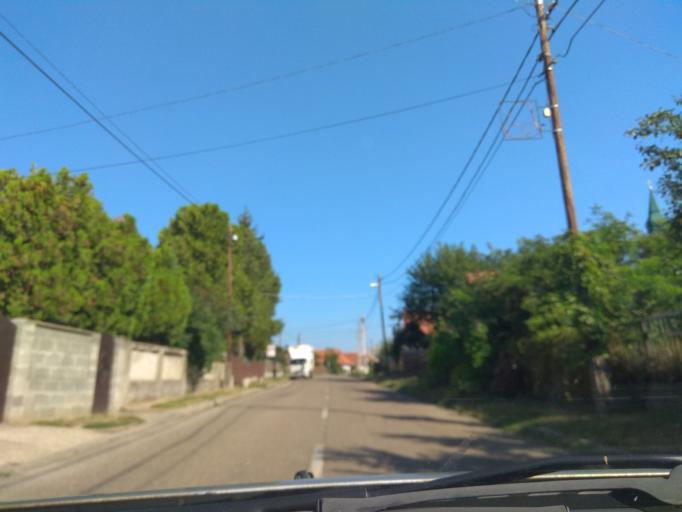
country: HU
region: Borsod-Abauj-Zemplen
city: Emod
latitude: 47.9456
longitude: 20.8125
